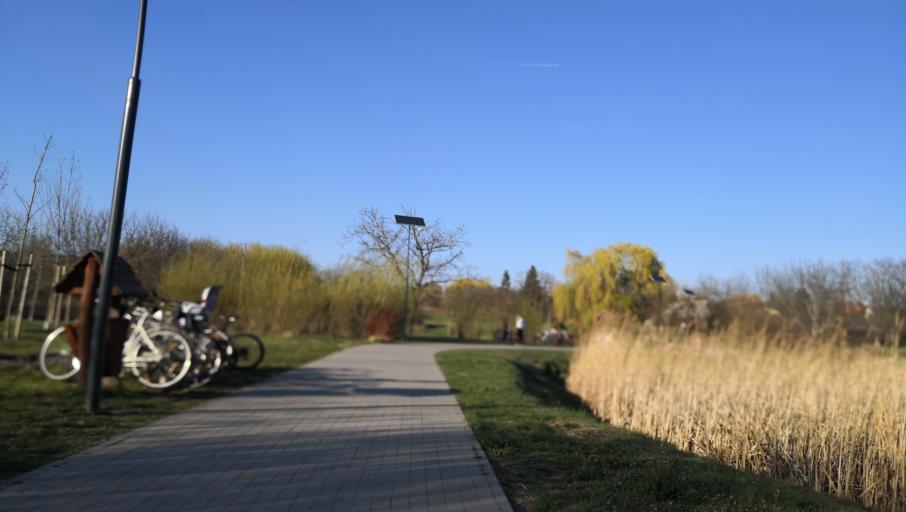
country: HU
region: Pest
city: Csomor
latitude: 47.5148
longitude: 19.2288
